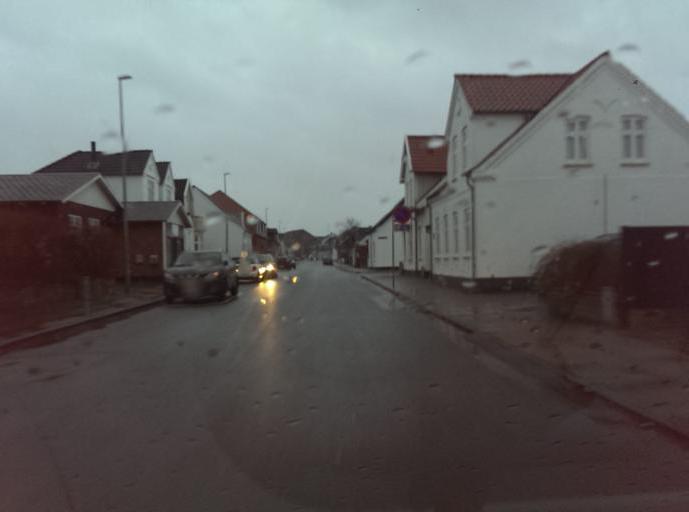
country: DK
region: South Denmark
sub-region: Esbjerg Kommune
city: Esbjerg
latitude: 55.4772
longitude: 8.4609
